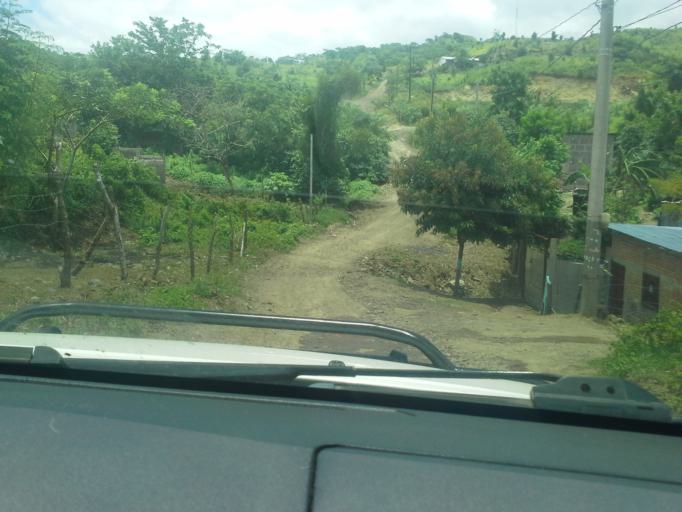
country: NI
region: Matagalpa
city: Ciudad Dario
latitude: 12.8618
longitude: -86.0863
